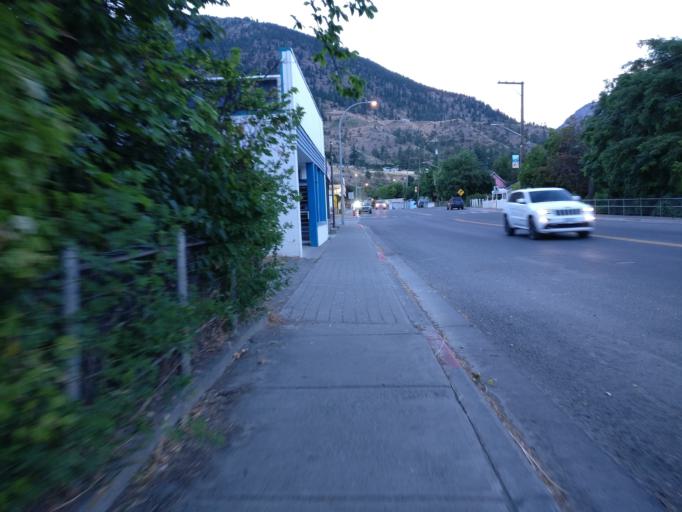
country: CA
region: British Columbia
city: Lillooet
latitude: 50.6897
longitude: -121.9374
